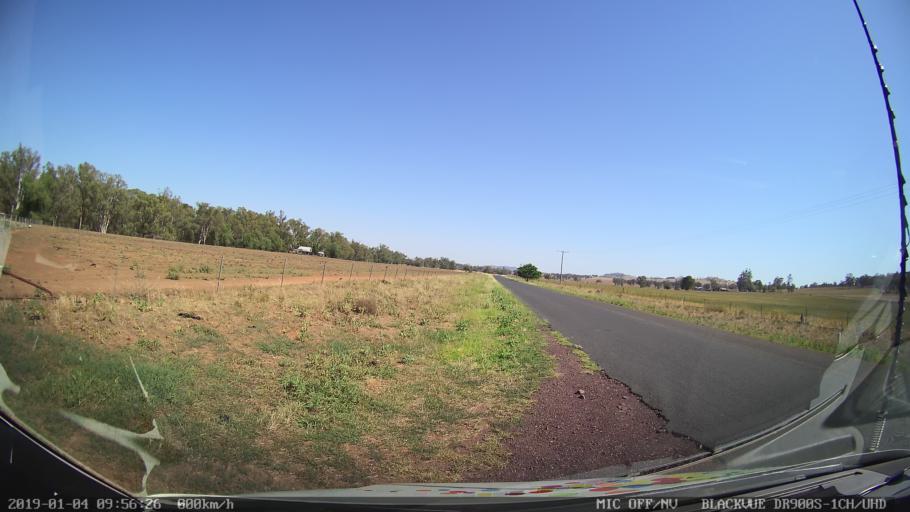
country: AU
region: New South Wales
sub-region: Cabonne
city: Canowindra
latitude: -33.5262
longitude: 148.3990
